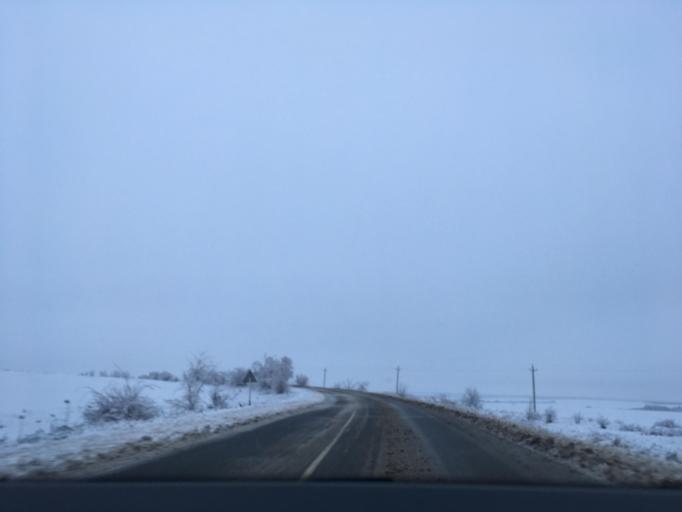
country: RU
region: Voronezj
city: Verkhniy Mamon
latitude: 50.0245
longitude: 40.0740
